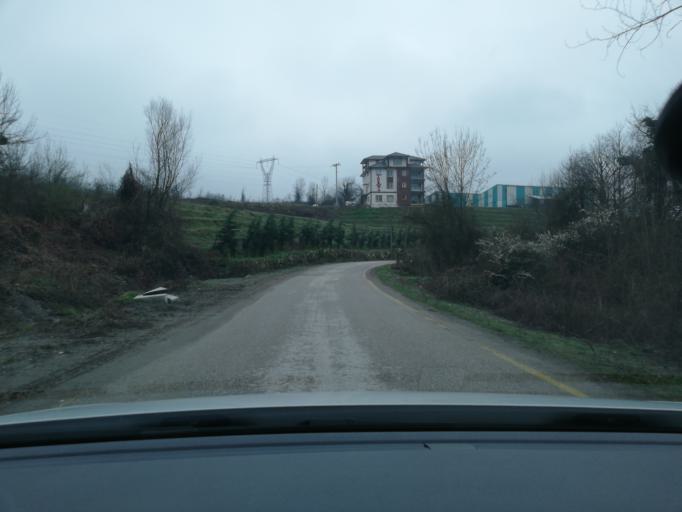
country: TR
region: Duzce
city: Kaynasli
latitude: 40.7729
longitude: 31.3556
